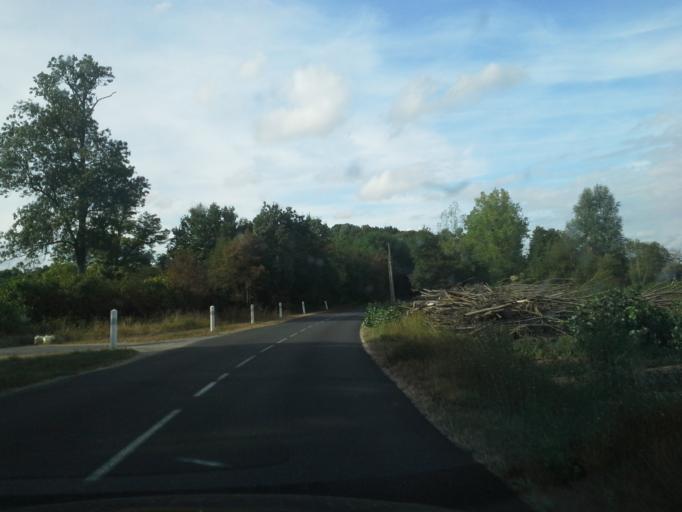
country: FR
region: Centre
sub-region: Departement d'Indre-et-Loire
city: Auzouer-en-Touraine
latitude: 47.5277
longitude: 0.9174
